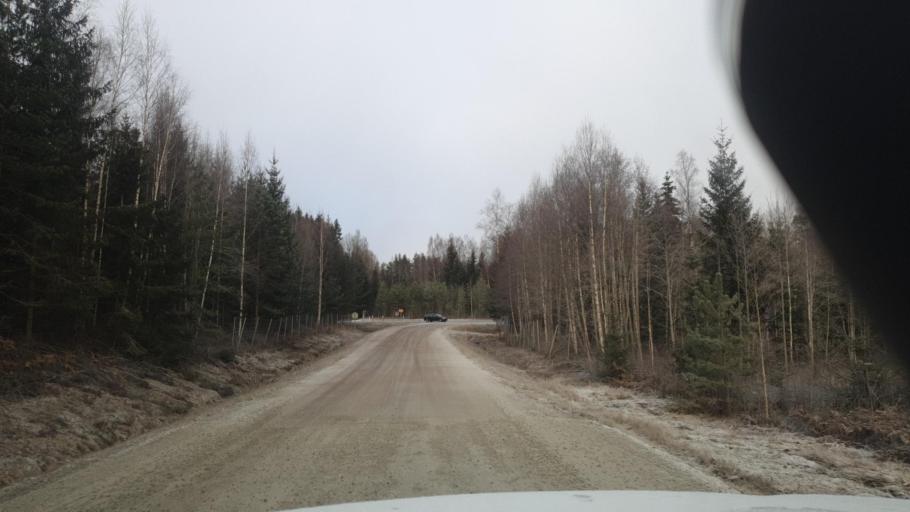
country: SE
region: Vaermland
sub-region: Karlstads Kommun
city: Edsvalla
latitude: 59.5106
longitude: 13.2075
